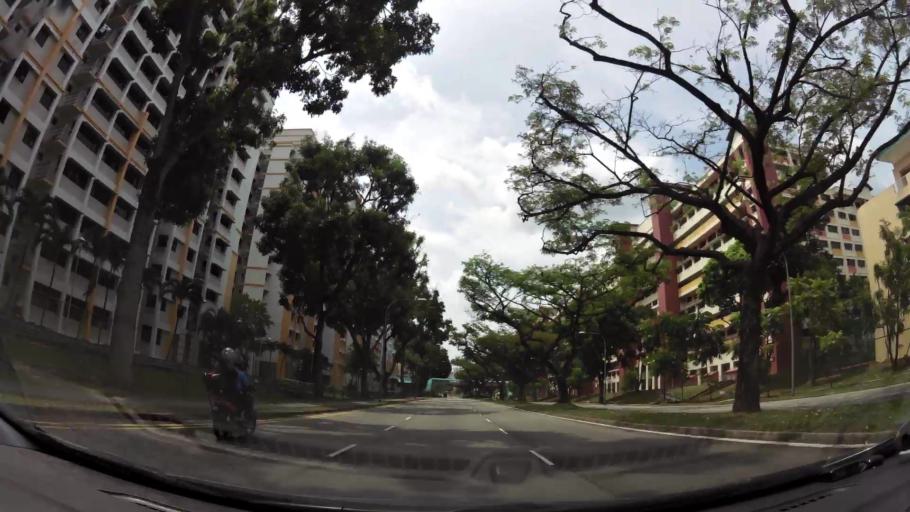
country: MY
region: Johor
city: Johor Bahru
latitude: 1.3439
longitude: 103.6992
